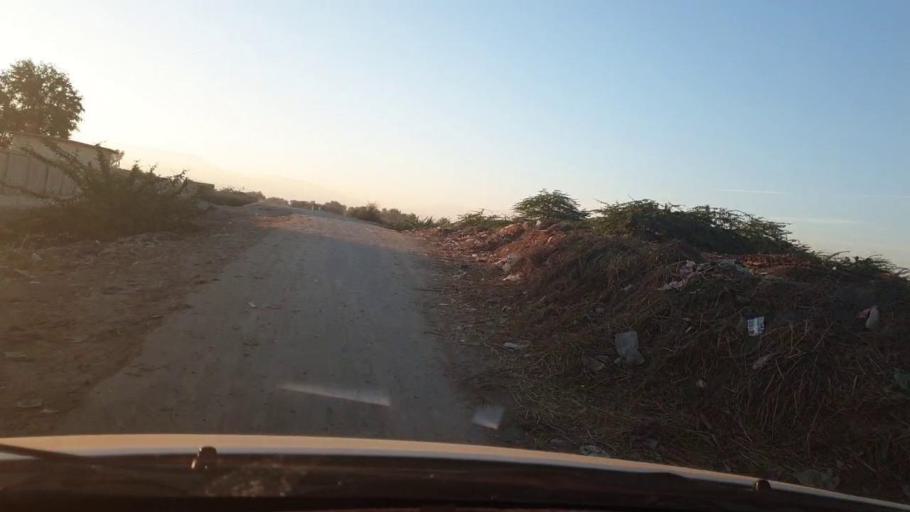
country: PK
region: Sindh
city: Johi
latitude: 26.8281
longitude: 67.4732
